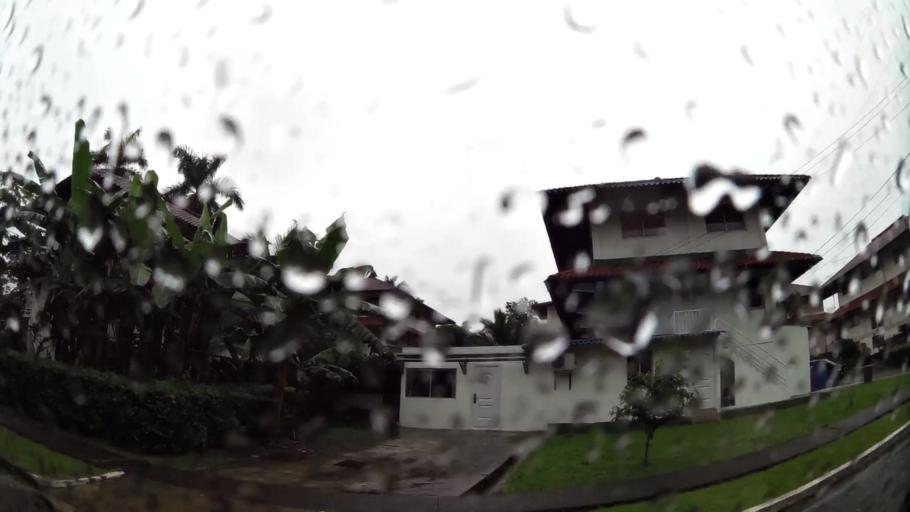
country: PA
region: Colon
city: Las Margaritas
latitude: 9.3111
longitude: -79.8752
